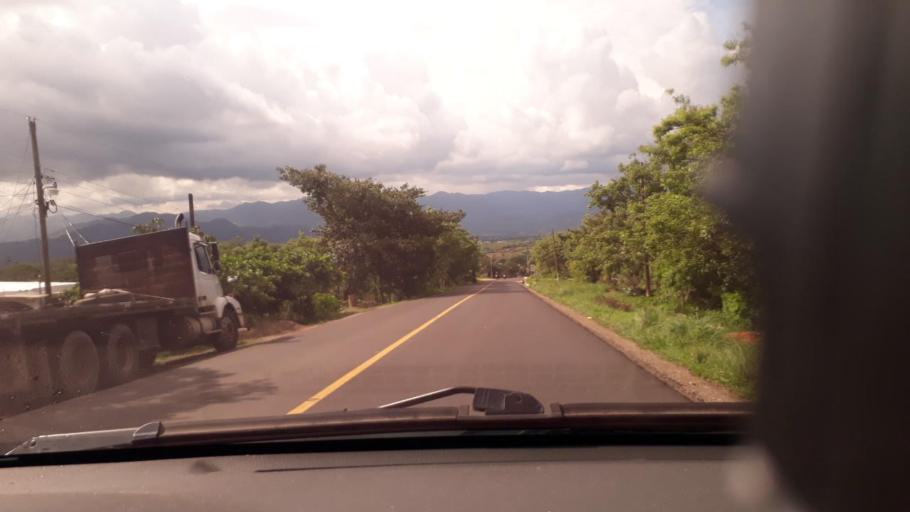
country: GT
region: Jutiapa
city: Quesada
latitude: 14.2291
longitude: -90.0253
